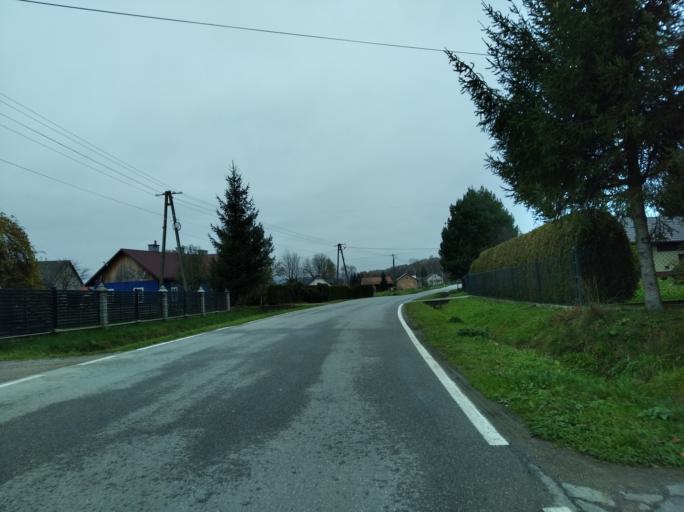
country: PL
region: Subcarpathian Voivodeship
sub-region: Powiat krosnienski
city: Leki
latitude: 49.8136
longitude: 21.6538
